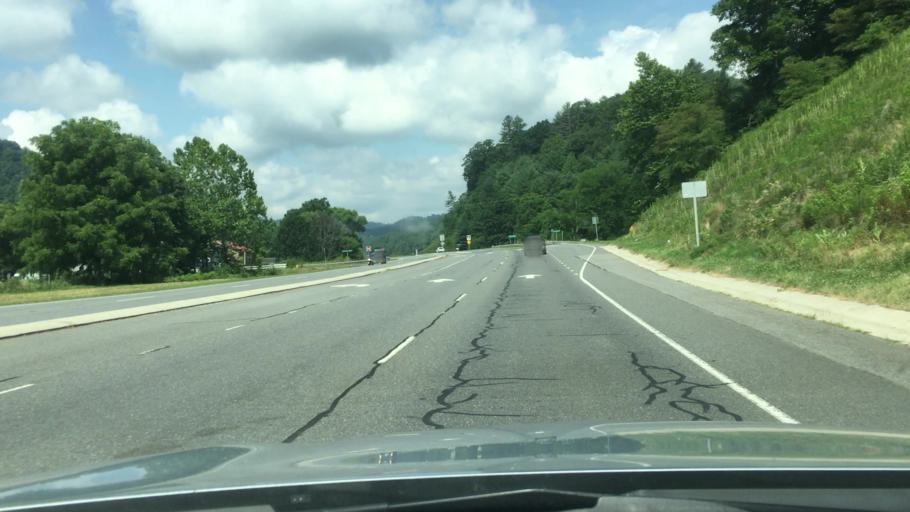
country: US
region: North Carolina
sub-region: Yancey County
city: Burnsville
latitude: 35.9139
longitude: -82.4199
